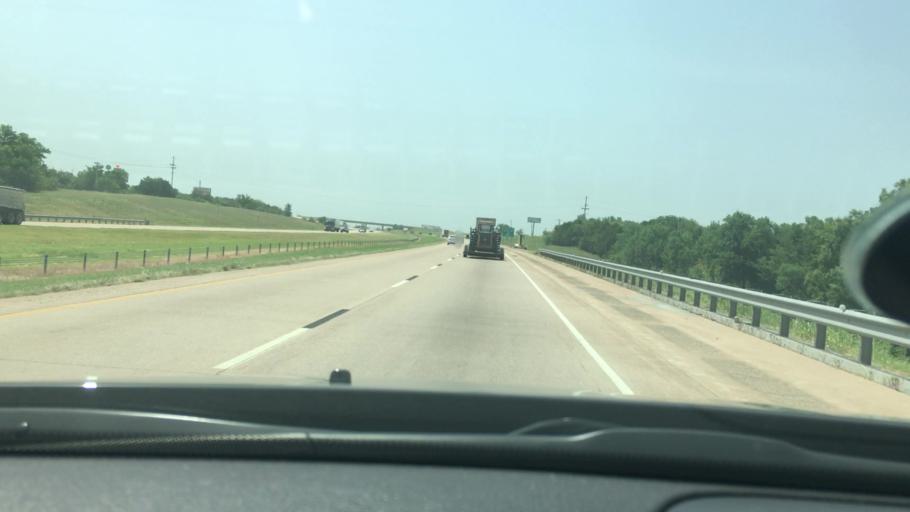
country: US
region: Oklahoma
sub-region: Garvin County
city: Pauls Valley
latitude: 34.7140
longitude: -97.2501
